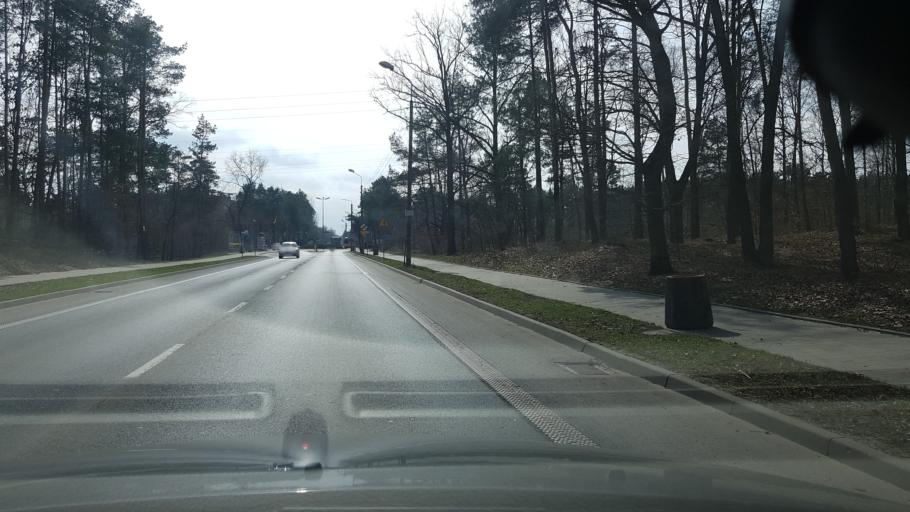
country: PL
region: Masovian Voivodeship
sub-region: Warszawa
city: Wesola
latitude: 52.2477
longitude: 21.2234
